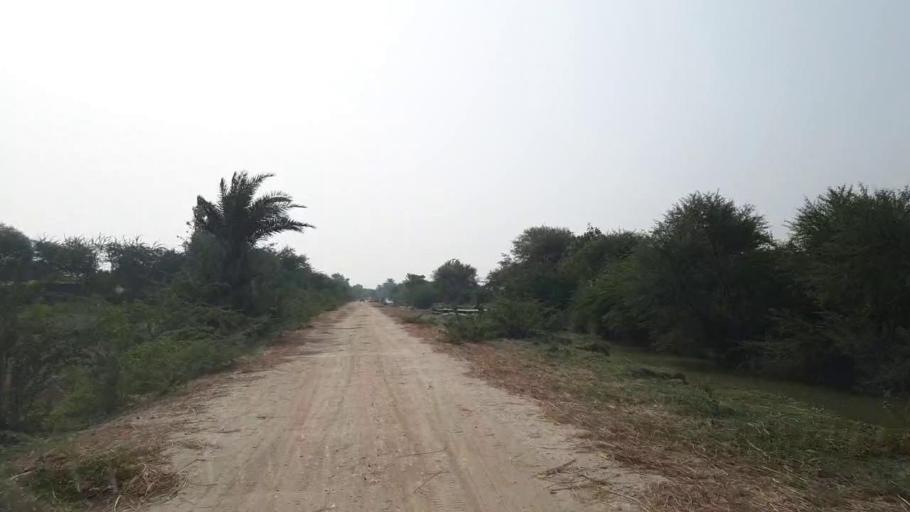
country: PK
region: Sindh
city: Kario
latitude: 24.7582
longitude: 68.5637
